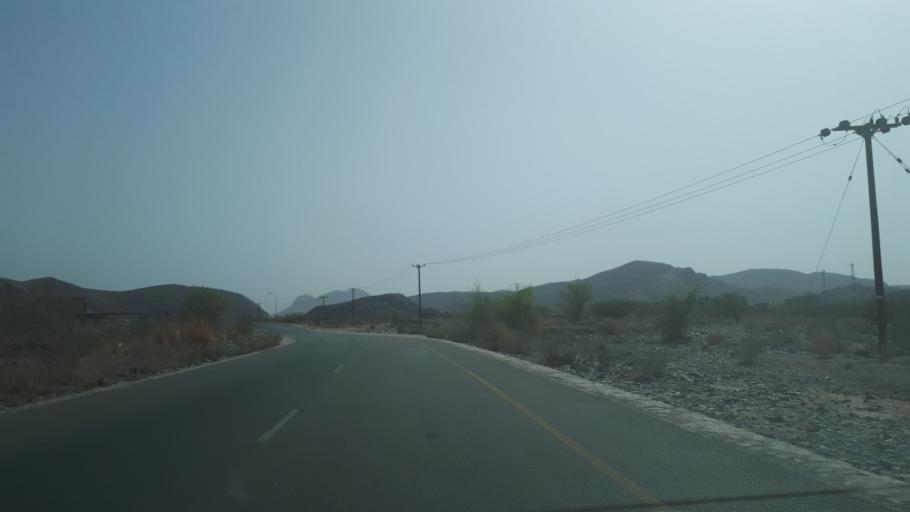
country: OM
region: Muhafazat ad Dakhiliyah
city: Bahla'
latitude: 23.2120
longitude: 56.9598
